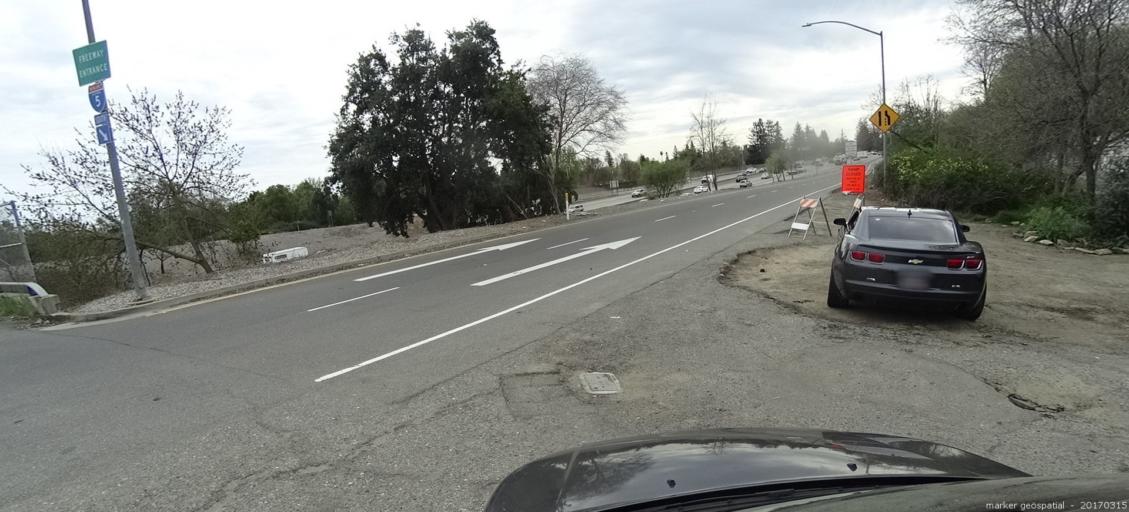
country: US
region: California
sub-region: Yolo County
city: West Sacramento
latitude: 38.5409
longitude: -121.5114
